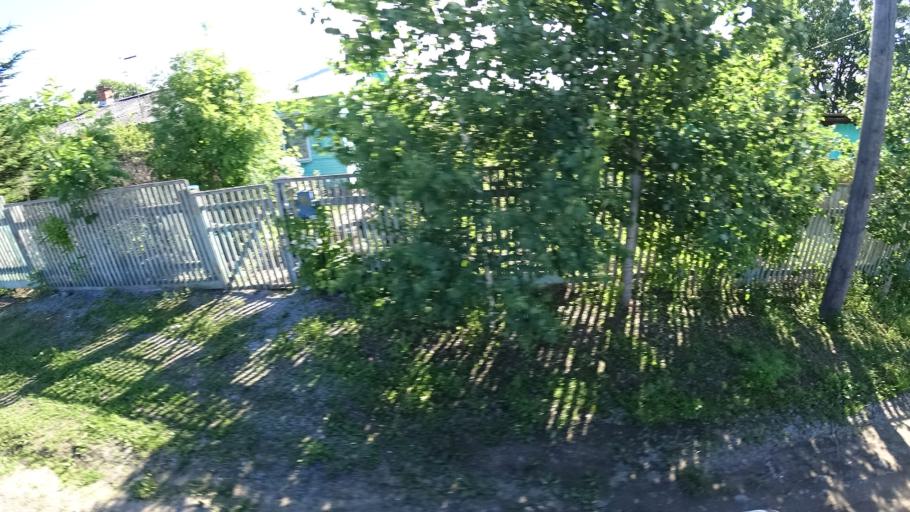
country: RU
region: Khabarovsk Krai
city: Khor
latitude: 47.8881
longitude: 134.9893
